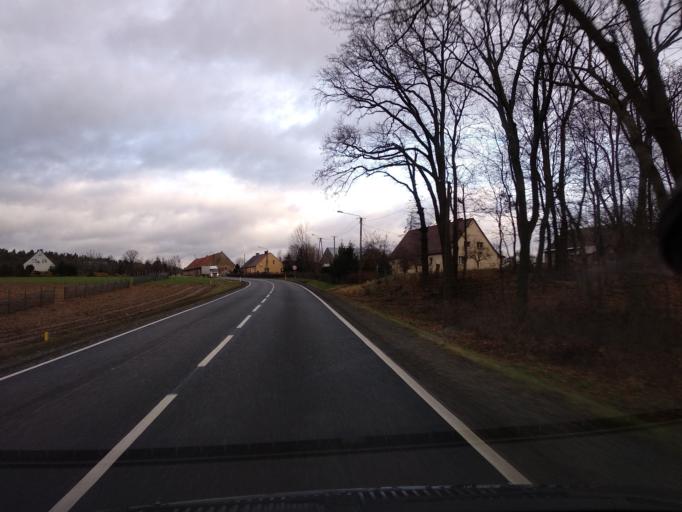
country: PL
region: Lower Silesian Voivodeship
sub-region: Powiat olesnicki
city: Miedzyborz
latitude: 51.3770
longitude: 17.6306
